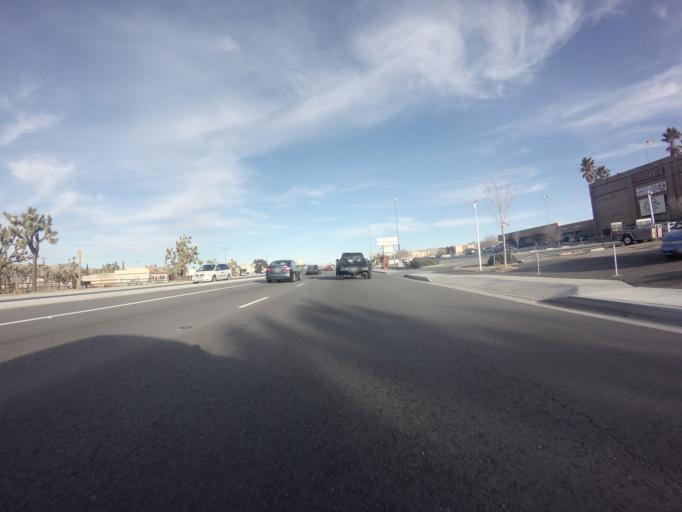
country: US
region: California
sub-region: San Bernardino County
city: Yucca Valley
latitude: 34.1205
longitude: -116.4288
